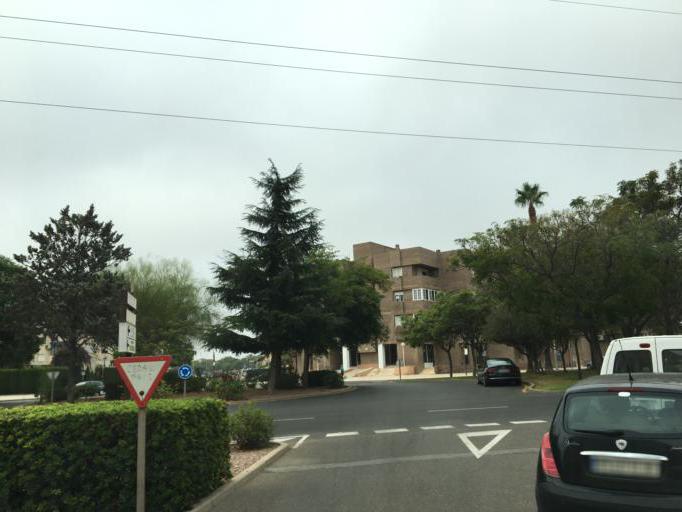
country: ES
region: Murcia
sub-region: Murcia
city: Cartagena
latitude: 37.6523
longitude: -1.0148
